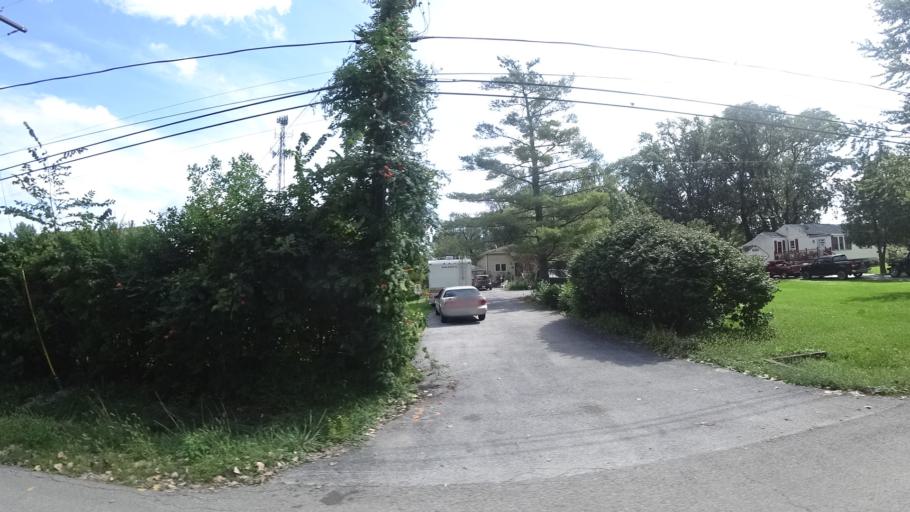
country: US
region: Illinois
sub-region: Cook County
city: Tinley Park
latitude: 41.5674
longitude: -87.7719
